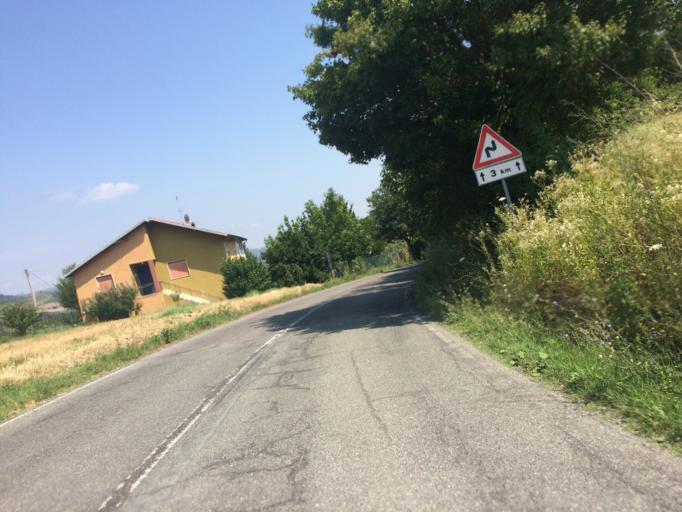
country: IT
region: Piedmont
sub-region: Provincia di Alessandria
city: Castelletto d'Erro
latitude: 44.6223
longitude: 8.4152
